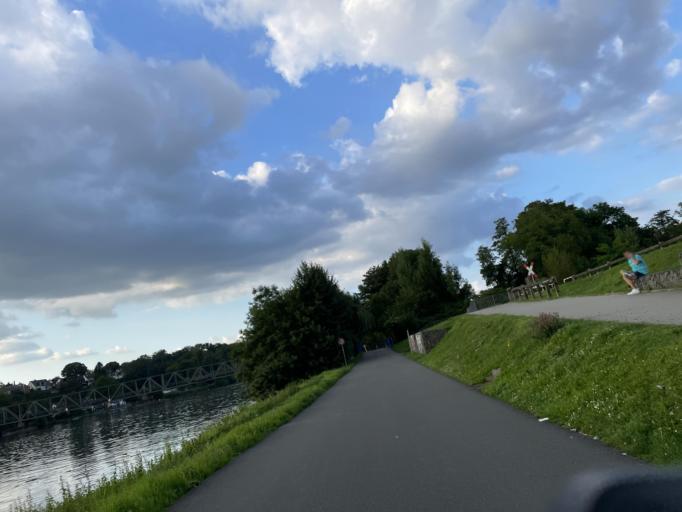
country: DE
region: North Rhine-Westphalia
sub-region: Regierungsbezirk Dusseldorf
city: Velbert
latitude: 51.3899
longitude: 7.0755
